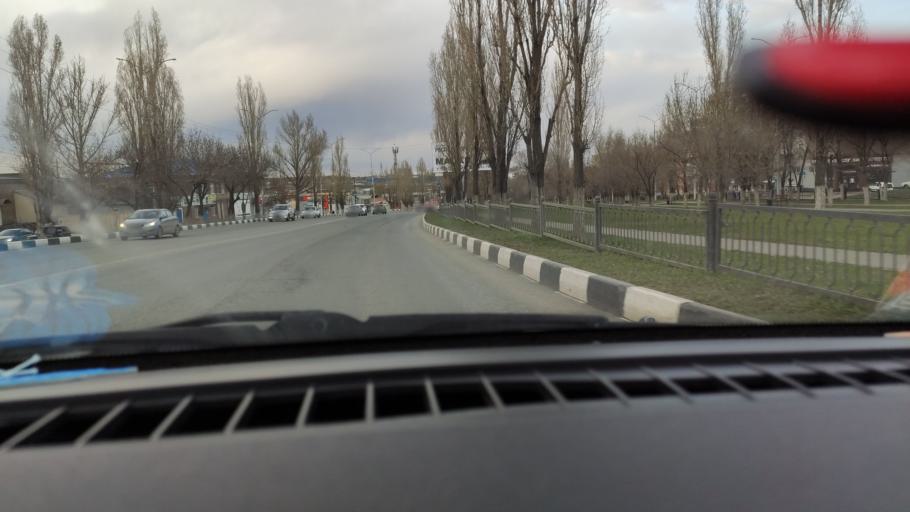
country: RU
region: Saratov
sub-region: Saratovskiy Rayon
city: Saratov
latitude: 51.6137
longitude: 45.9711
